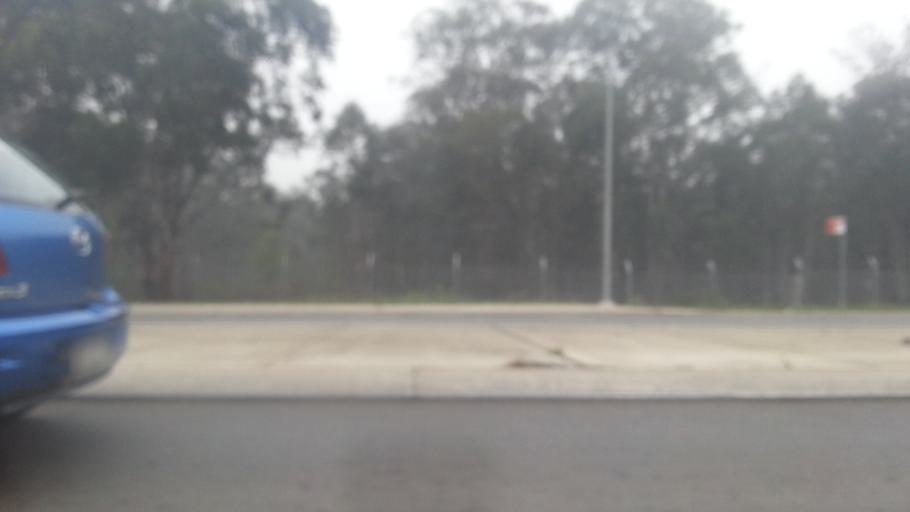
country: AU
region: New South Wales
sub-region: Penrith Municipality
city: Werrington Downs
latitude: -33.7304
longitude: 150.7190
